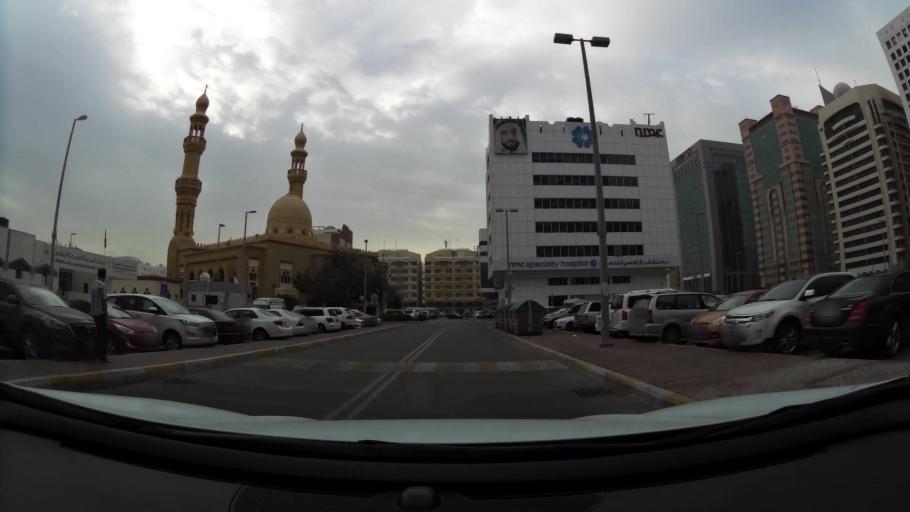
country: AE
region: Abu Dhabi
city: Abu Dhabi
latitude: 24.4831
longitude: 54.3612
